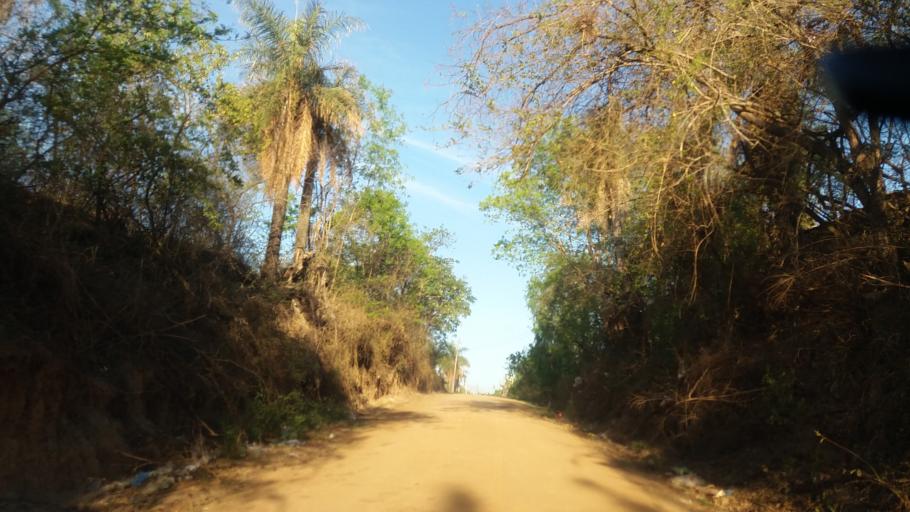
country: AR
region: Corrientes
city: Corrientes
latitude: -27.5163
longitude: -58.8314
